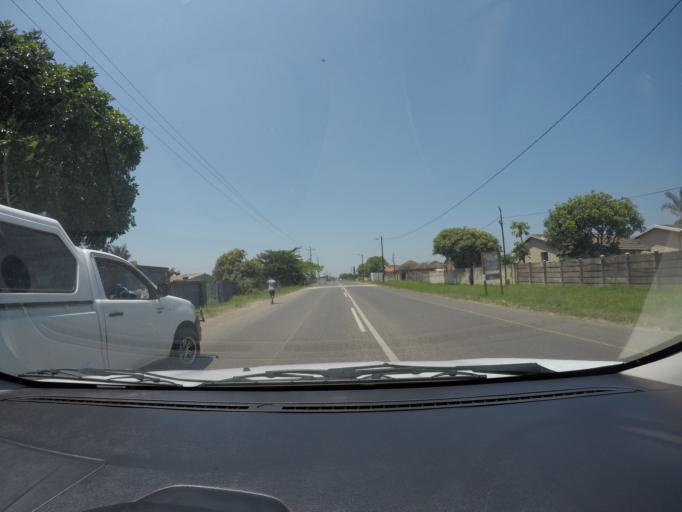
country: ZA
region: KwaZulu-Natal
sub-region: uThungulu District Municipality
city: eSikhawini
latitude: -28.8872
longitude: 31.8837
